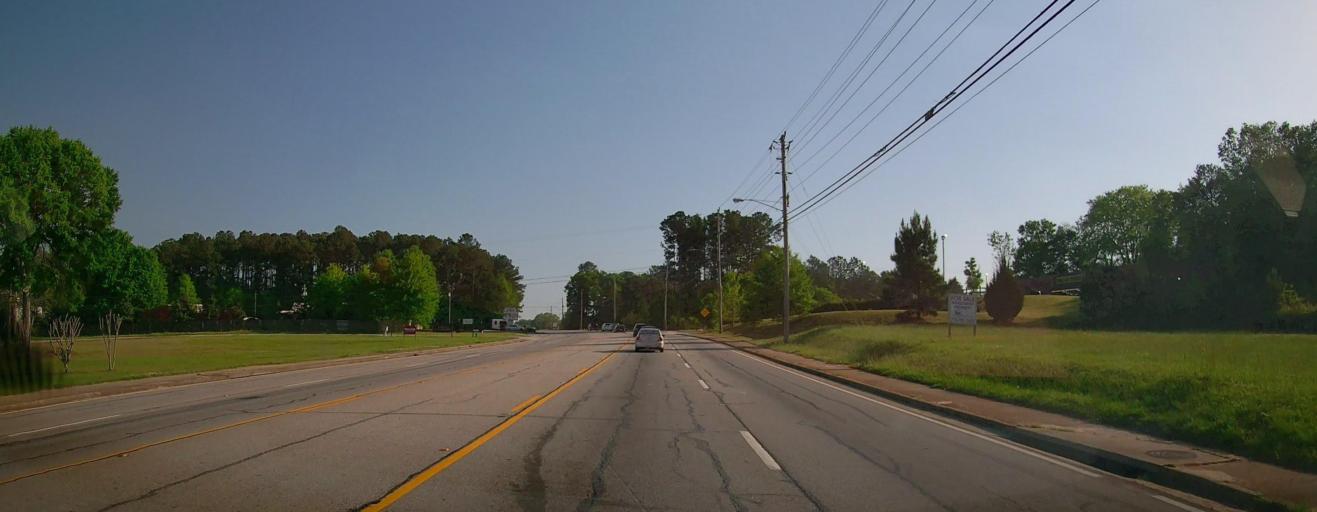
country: US
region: Georgia
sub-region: Newton County
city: Covington
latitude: 33.5886
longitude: -83.8768
